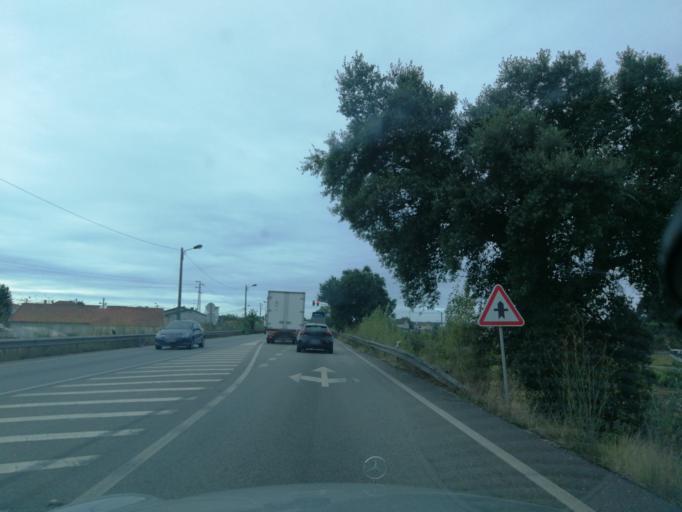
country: PT
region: Aveiro
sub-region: Agueda
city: Valongo
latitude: 40.6195
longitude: -8.4621
